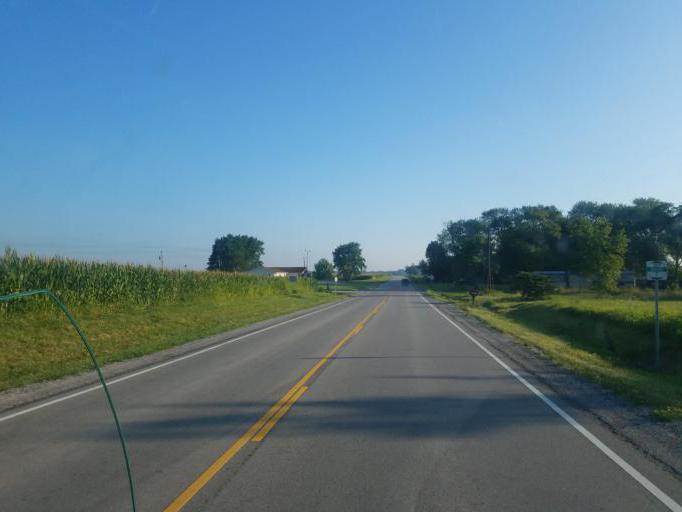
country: US
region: Illinois
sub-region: Bond County
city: Greenville
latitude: 38.8428
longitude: -89.3712
